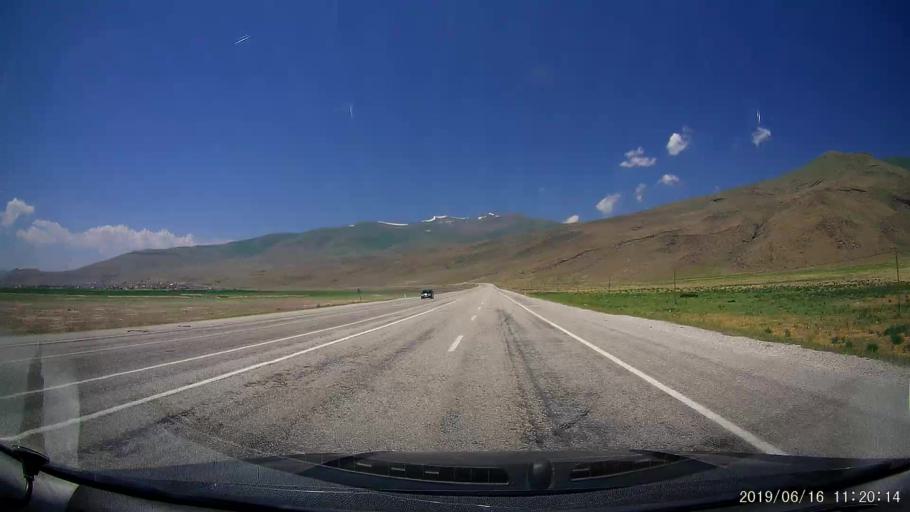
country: TR
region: Agri
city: Dogubayazit
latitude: 39.6980
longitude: 44.0955
